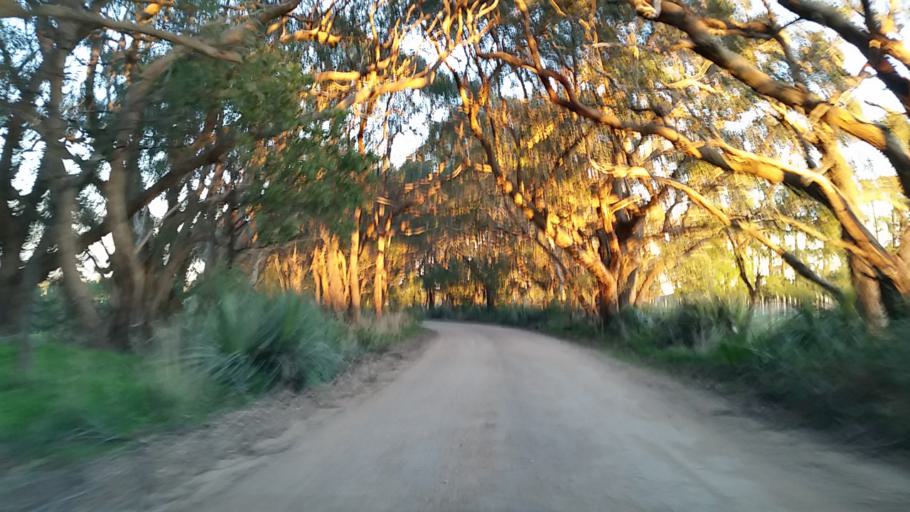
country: AU
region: South Australia
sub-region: Alexandrina
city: Mount Compass
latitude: -35.2846
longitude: 138.6001
